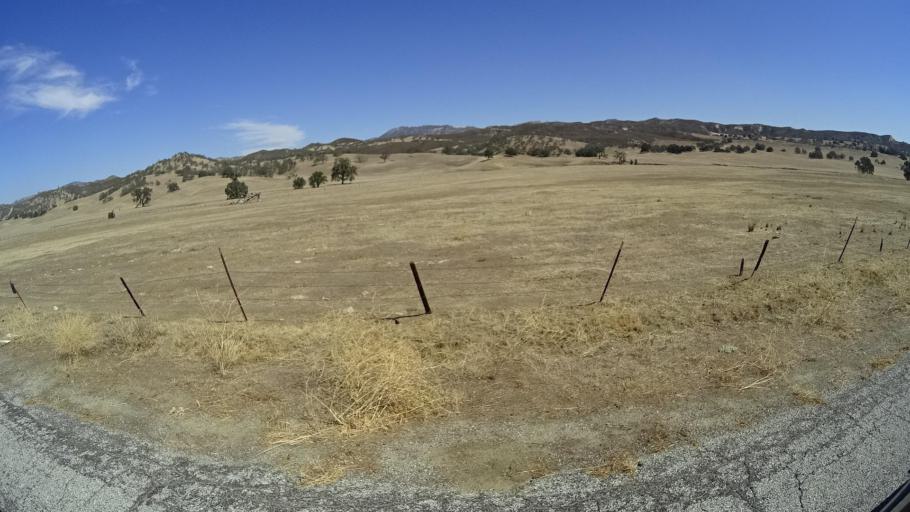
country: US
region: California
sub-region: San Luis Obispo County
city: San Miguel
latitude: 36.0342
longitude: -120.6628
